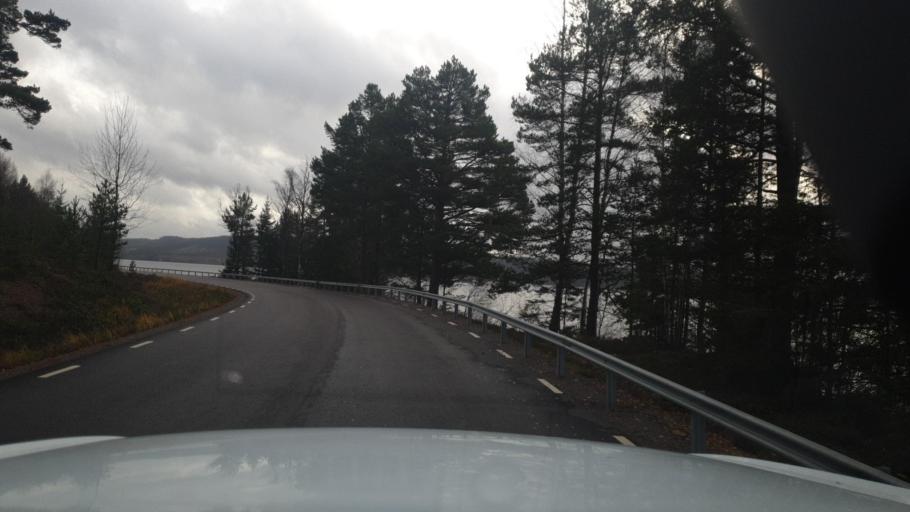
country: SE
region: Vaermland
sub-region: Torsby Kommun
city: Torsby
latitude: 59.9868
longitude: 12.7866
